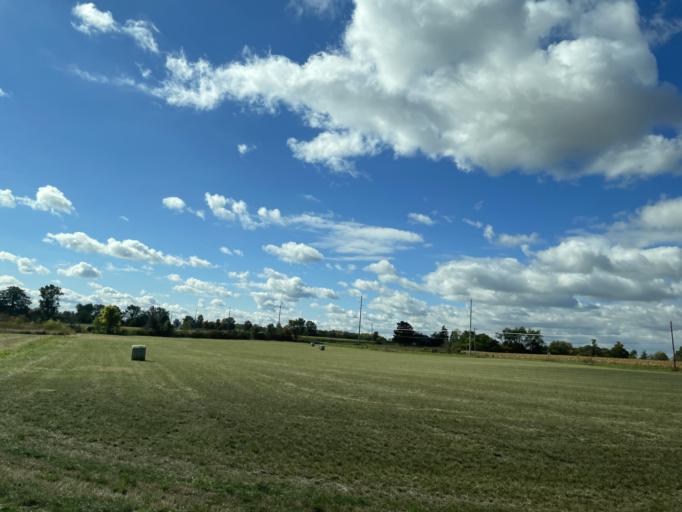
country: US
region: Indiana
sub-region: Allen County
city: Fort Wayne
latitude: 41.1125
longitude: -85.2252
